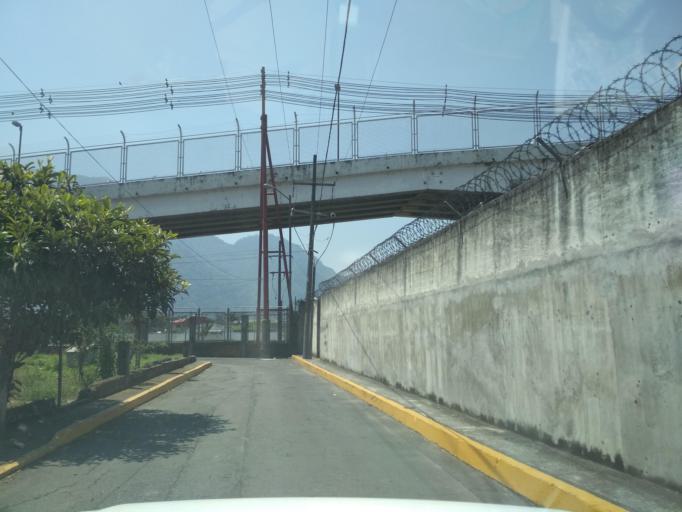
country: MX
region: Veracruz
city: Orizaba
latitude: 18.8373
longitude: -97.1088
